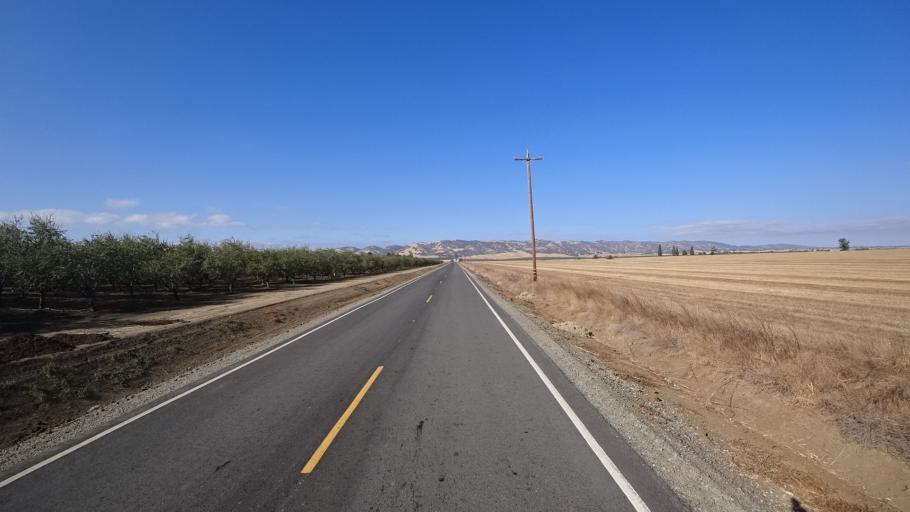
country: US
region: California
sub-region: Yolo County
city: Esparto
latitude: 38.7811
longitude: -122.0374
